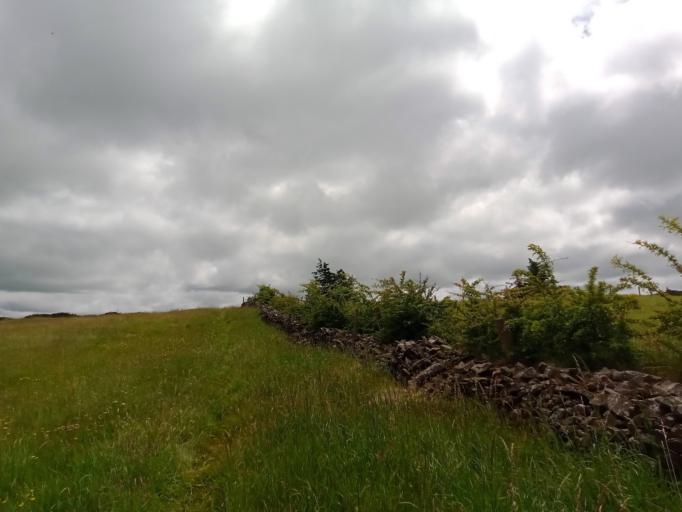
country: IE
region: Leinster
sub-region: Laois
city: Rathdowney
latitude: 52.7985
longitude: -7.4714
